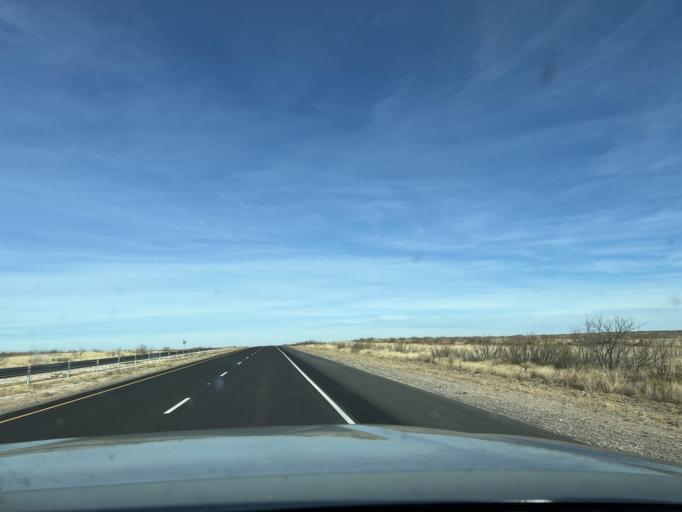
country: US
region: Texas
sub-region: Ector County
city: Gardendale
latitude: 32.0327
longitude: -102.4332
